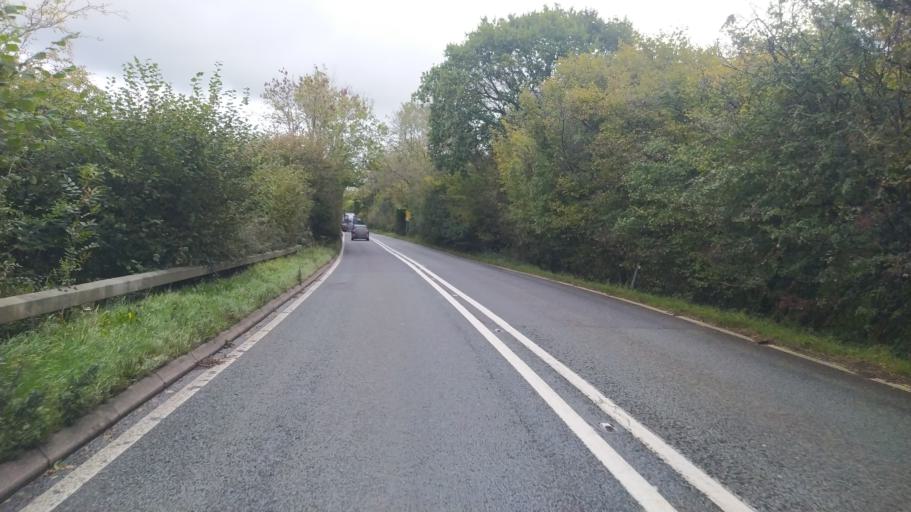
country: GB
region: England
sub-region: Dorset
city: Lyme Regis
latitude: 50.7429
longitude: -2.8640
